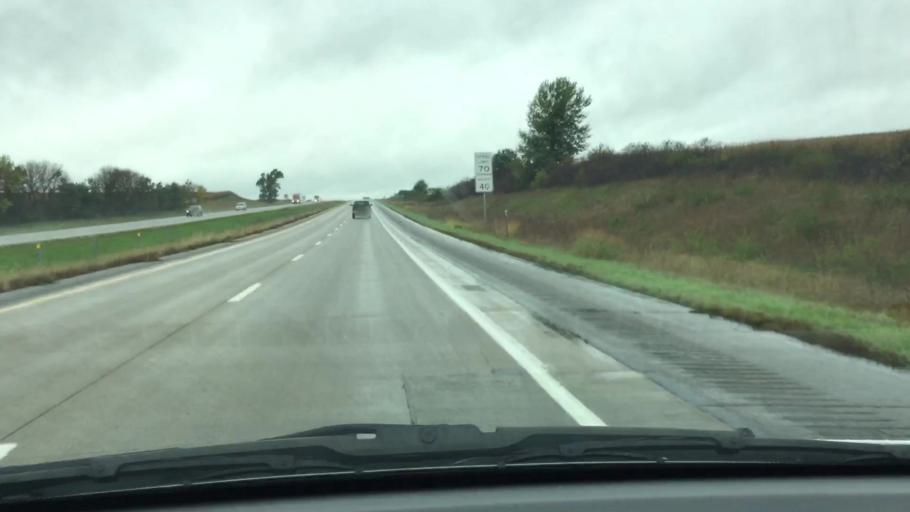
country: US
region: Iowa
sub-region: Jasper County
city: Newton
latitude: 41.6817
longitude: -92.9165
